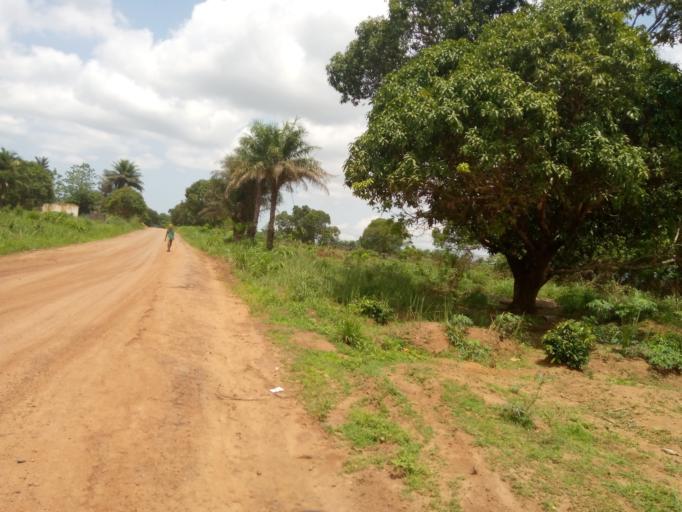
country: SL
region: Western Area
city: Waterloo
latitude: 8.3828
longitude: -12.9577
